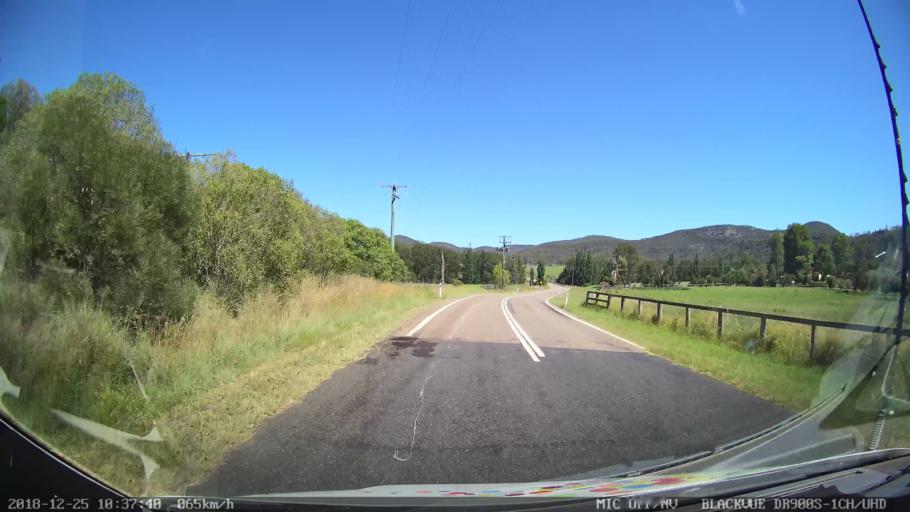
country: AU
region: New South Wales
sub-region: Upper Hunter Shire
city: Merriwa
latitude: -32.4081
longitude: 150.3759
